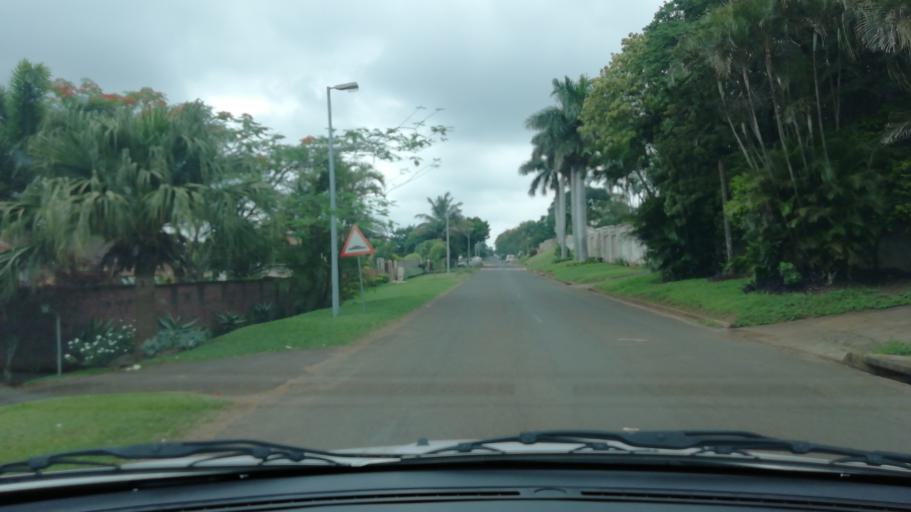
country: ZA
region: KwaZulu-Natal
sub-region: uThungulu District Municipality
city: Empangeni
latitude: -28.7661
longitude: 31.9028
